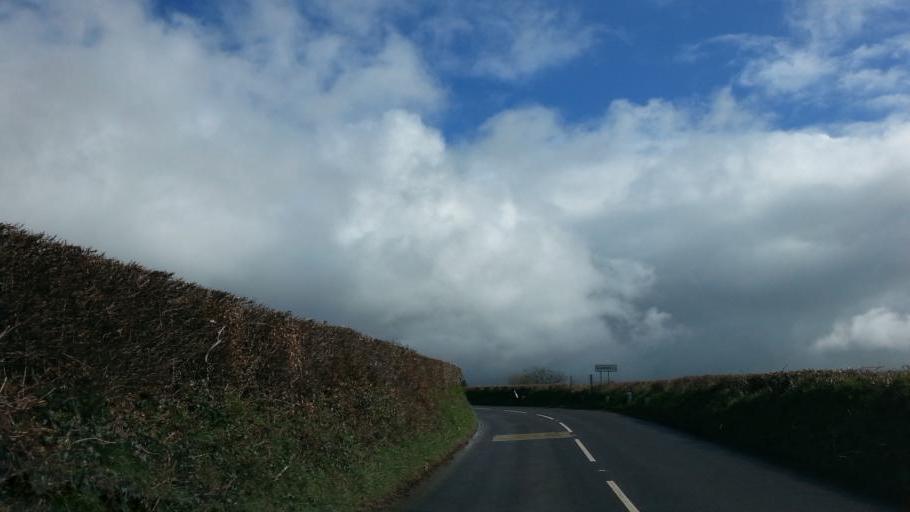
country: GB
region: England
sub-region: Devon
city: Barnstaple
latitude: 51.1104
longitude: -4.0202
